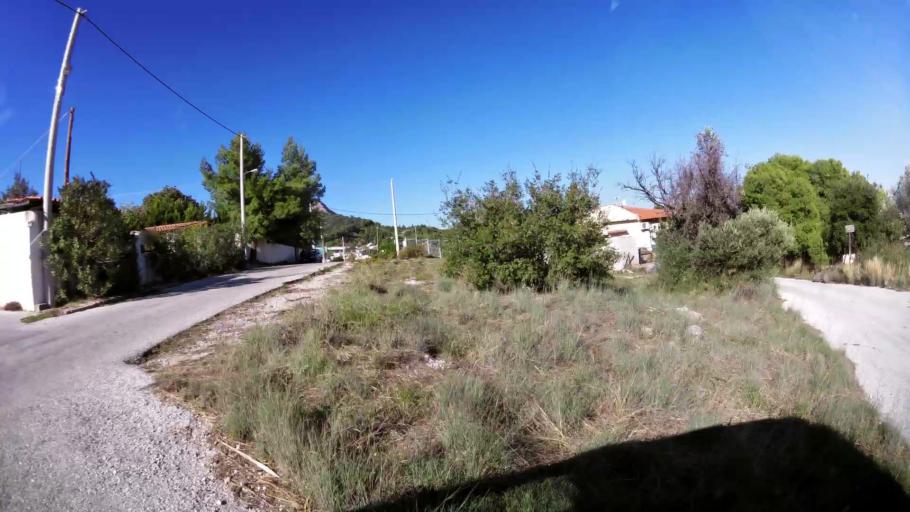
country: GR
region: Attica
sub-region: Nomarchia Anatolikis Attikis
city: Leondarion
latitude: 37.9960
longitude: 23.8447
